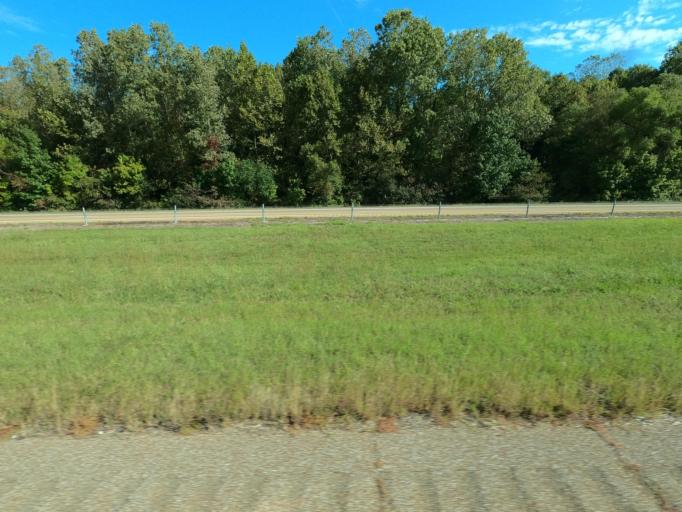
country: US
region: Tennessee
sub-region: Shelby County
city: Millington
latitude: 35.3143
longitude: -89.8652
